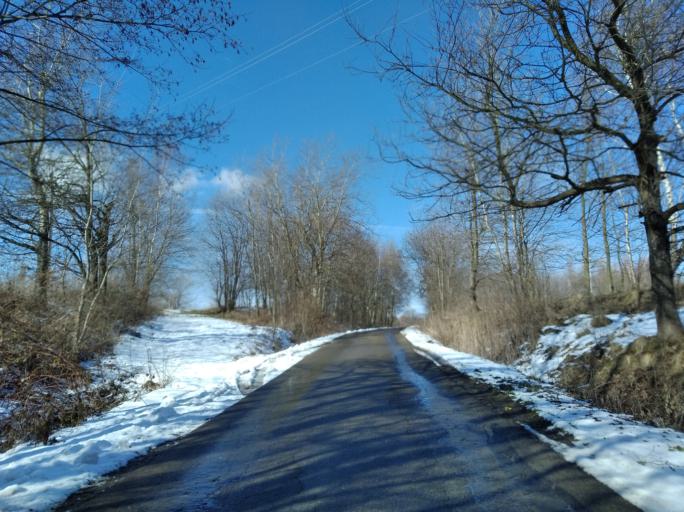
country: PL
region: Subcarpathian Voivodeship
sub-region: Powiat brzozowski
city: Jablonica Polska
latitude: 49.7271
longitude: 21.8745
